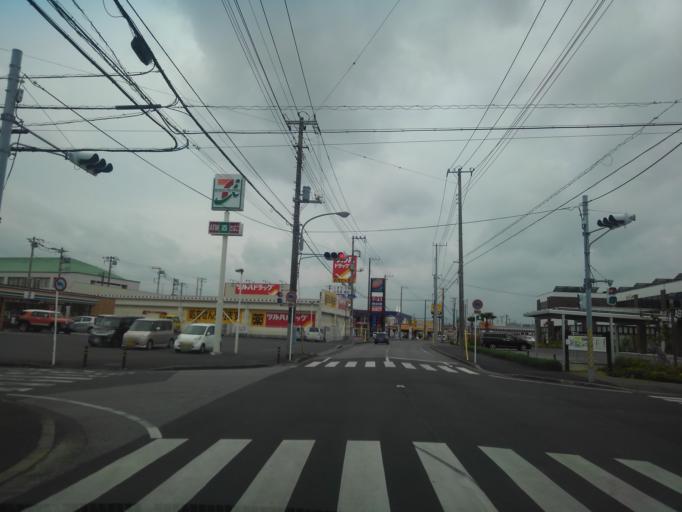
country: JP
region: Chiba
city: Kimitsu
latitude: 35.3261
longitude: 139.9211
